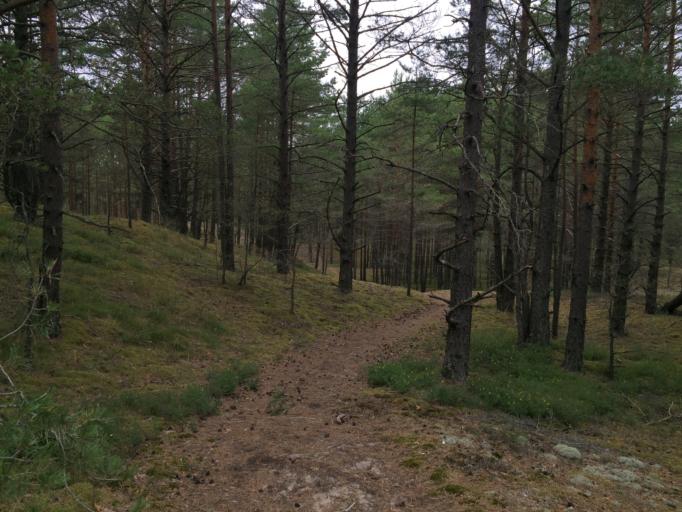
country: LV
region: Riga
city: Jaunciems
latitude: 57.1029
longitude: 24.1824
